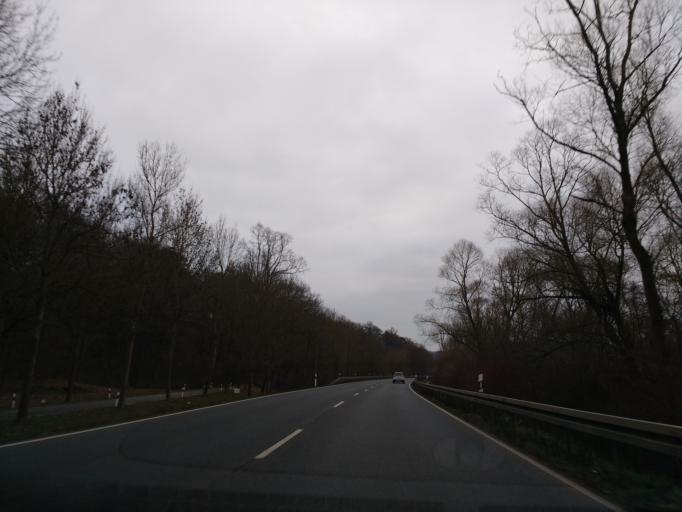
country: DE
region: Hesse
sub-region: Regierungsbezirk Kassel
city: Alheim
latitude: 51.0211
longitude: 9.6871
